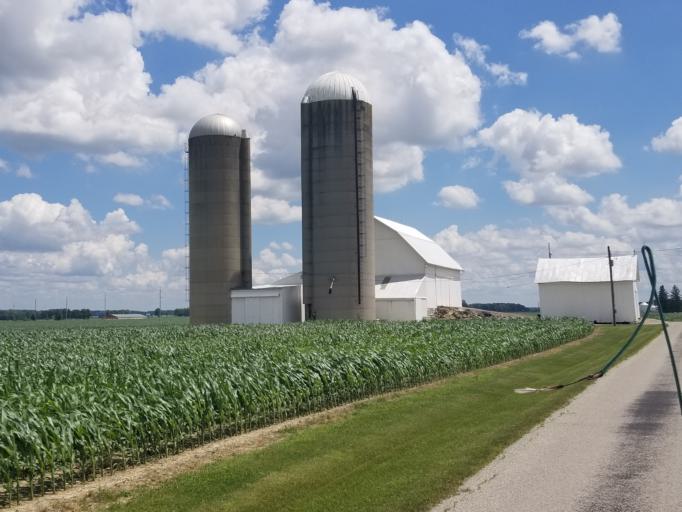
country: US
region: Ohio
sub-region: Huron County
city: Willard
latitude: 40.9420
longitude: -82.8257
